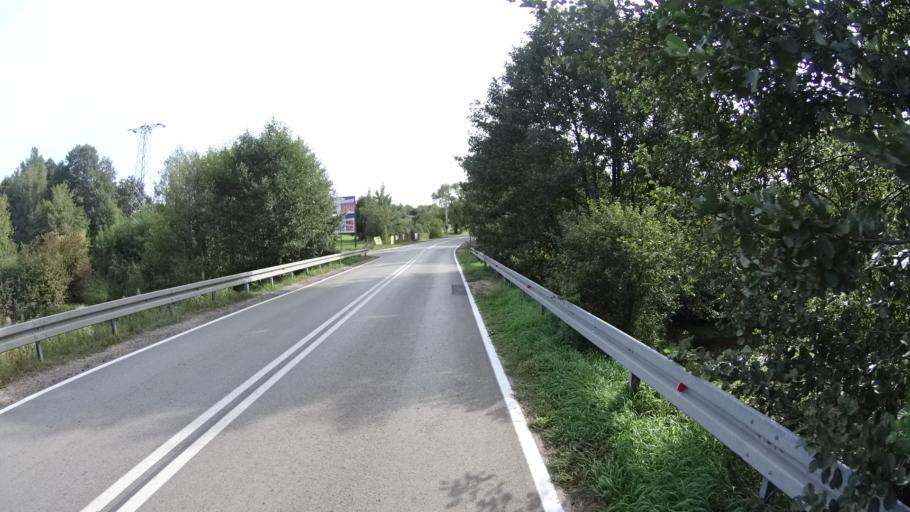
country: PL
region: Masovian Voivodeship
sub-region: Powiat legionowski
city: Serock
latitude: 52.4764
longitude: 21.0926
